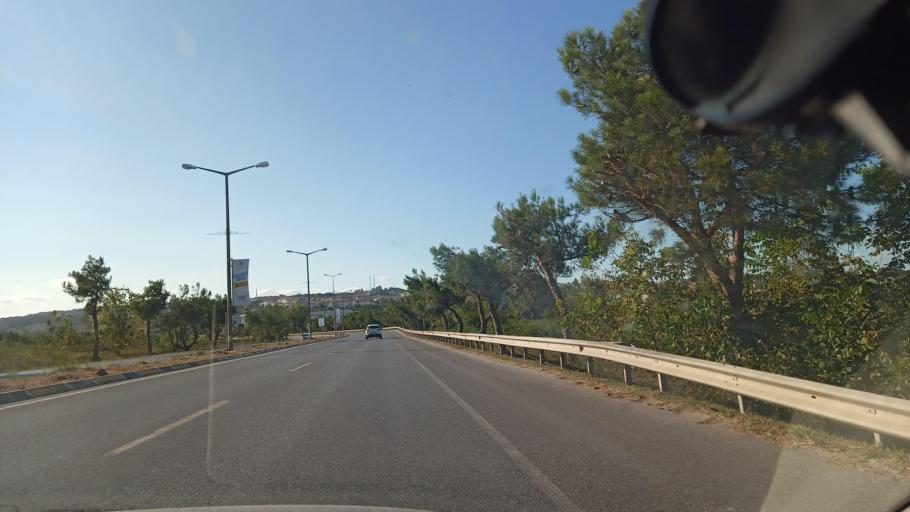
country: TR
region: Sakarya
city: Kazimpasa
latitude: 40.8471
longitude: 30.3258
